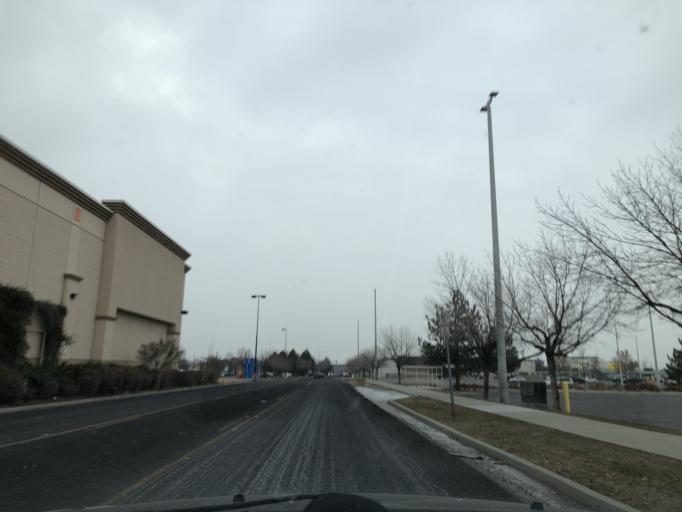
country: US
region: Utah
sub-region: Cache County
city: Logan
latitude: 41.7542
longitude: -111.8308
